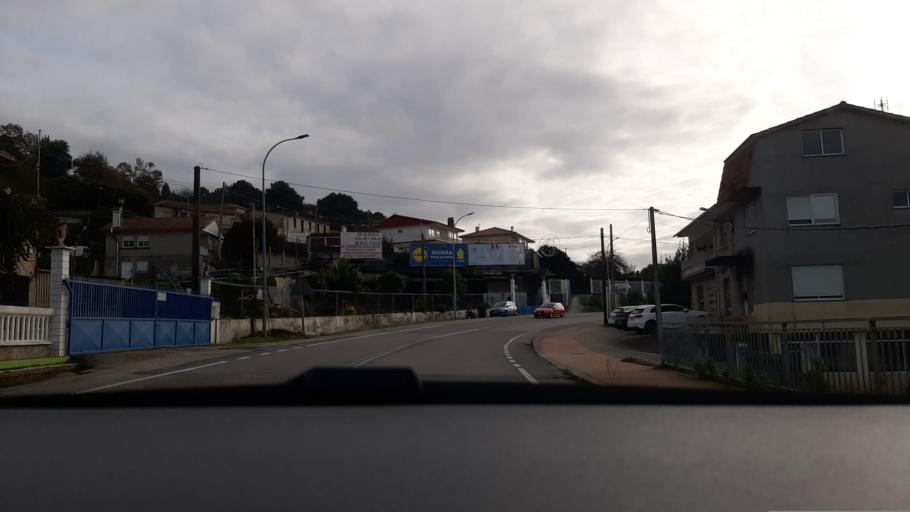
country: ES
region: Galicia
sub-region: Provincia de Pontevedra
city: Nigran
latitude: 42.1653
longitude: -8.8014
